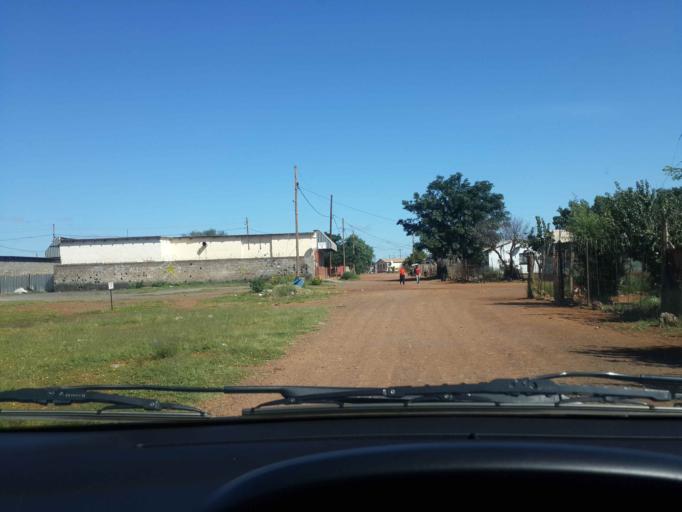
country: ZA
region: Northern Cape
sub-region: Siyanda District Municipality
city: Danielskuil
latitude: -28.1928
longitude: 23.5367
